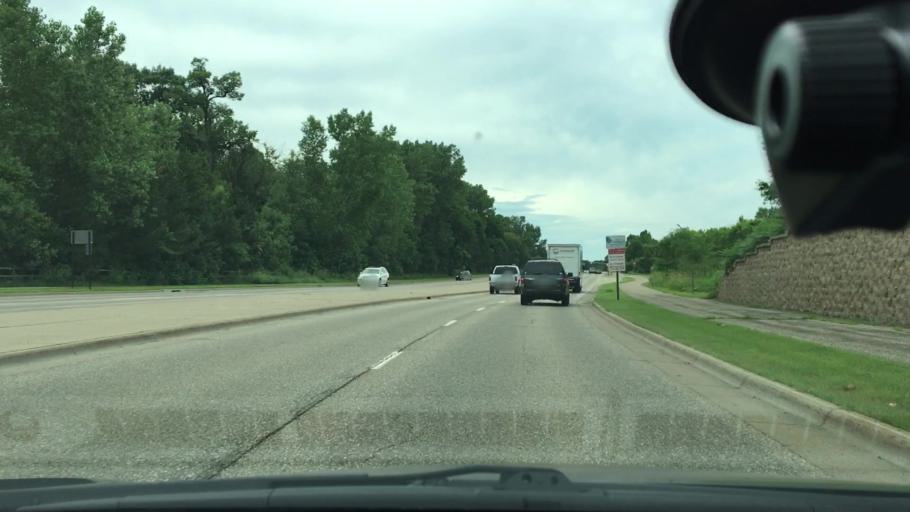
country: US
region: Minnesota
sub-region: Hennepin County
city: Maple Grove
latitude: 45.0655
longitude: -93.4332
